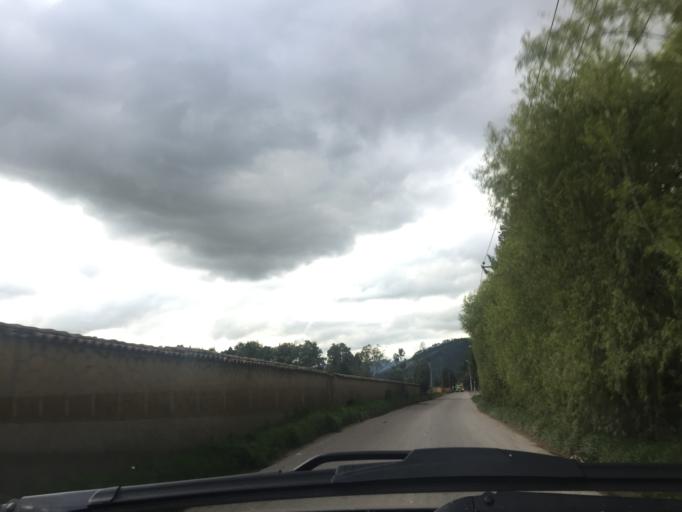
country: CO
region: Cundinamarca
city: Sopo
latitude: 4.9368
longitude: -73.9435
